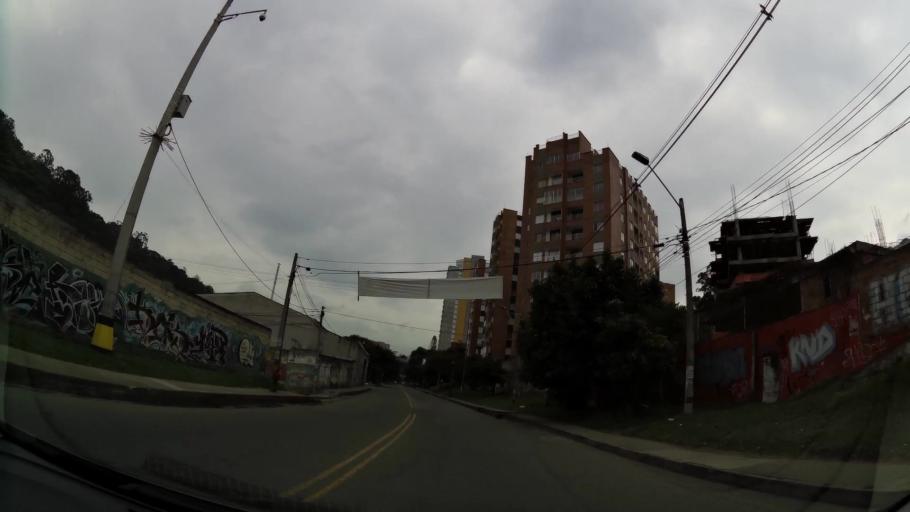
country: CO
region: Antioquia
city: Medellin
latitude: 6.2735
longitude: -75.5835
